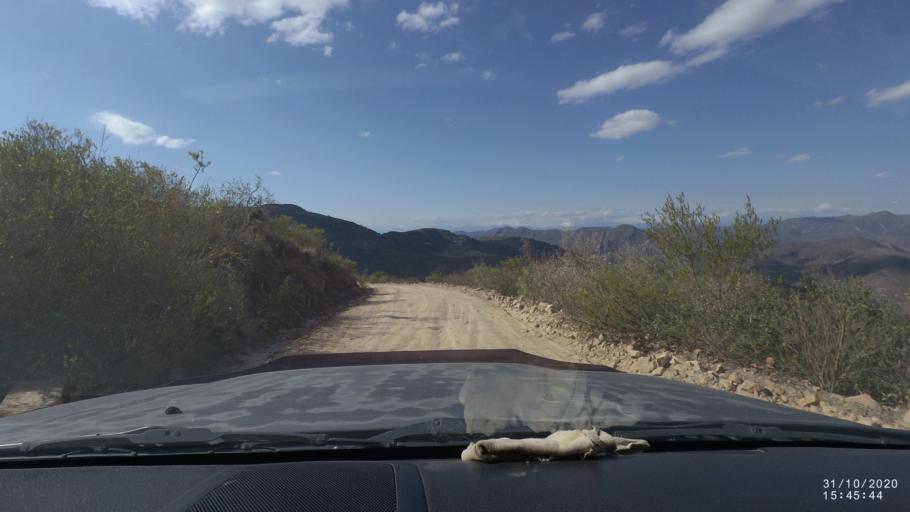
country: BO
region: Chuquisaca
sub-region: Provincia Zudanez
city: Mojocoya
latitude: -18.3175
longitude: -64.7170
